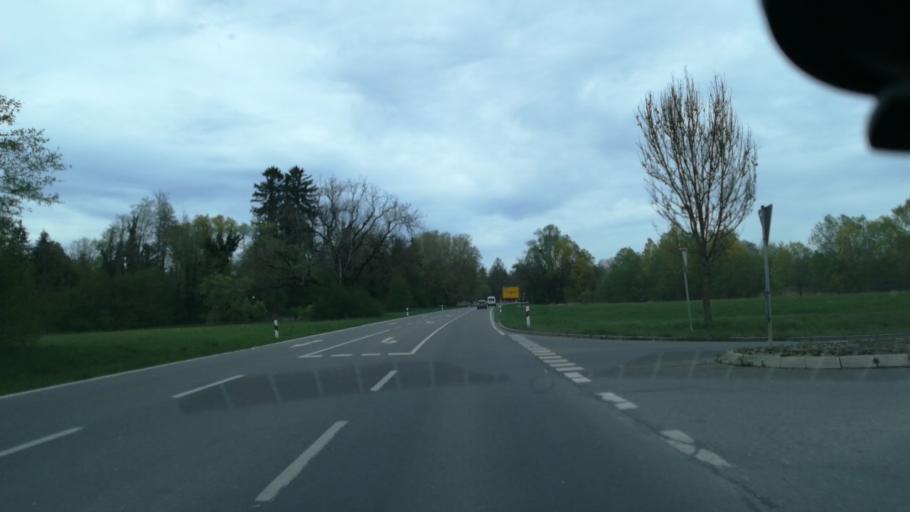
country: DE
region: Baden-Wuerttemberg
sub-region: Freiburg Region
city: Moos
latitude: 47.7500
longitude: 8.9230
